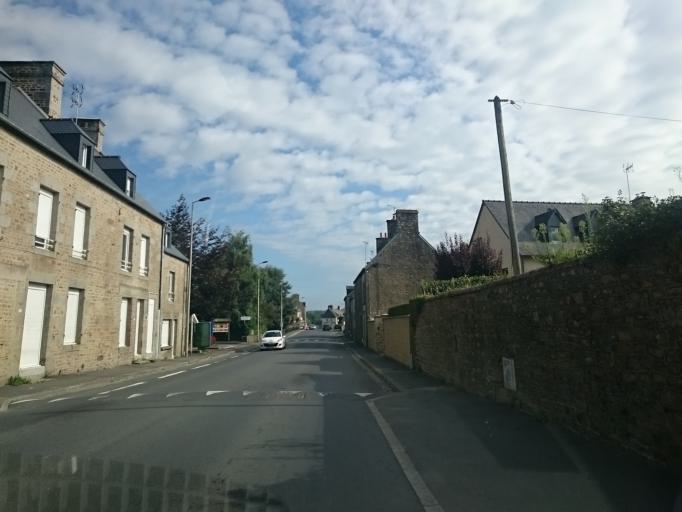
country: FR
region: Lower Normandy
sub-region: Departement de la Manche
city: Saint-Senier-sous-Avranches
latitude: 48.6966
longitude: -1.3467
